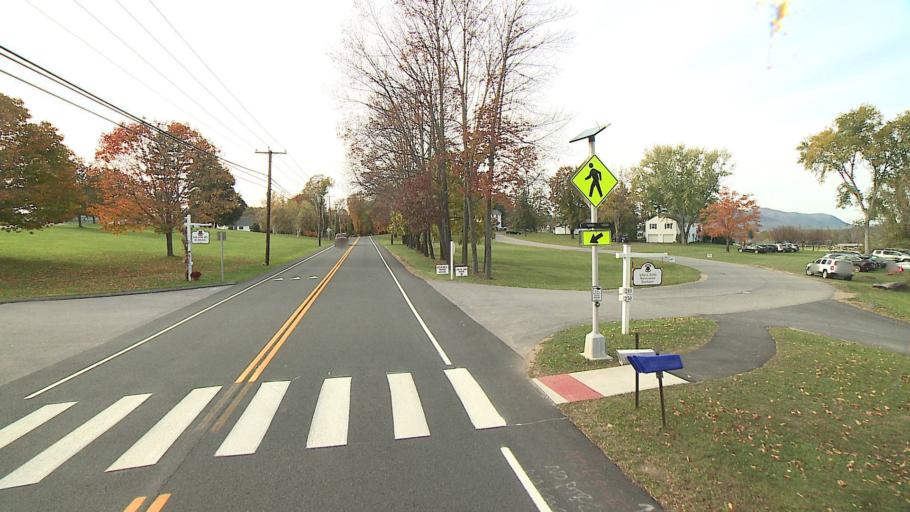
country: US
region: Connecticut
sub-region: Litchfield County
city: Canaan
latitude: 42.0004
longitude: -73.3910
